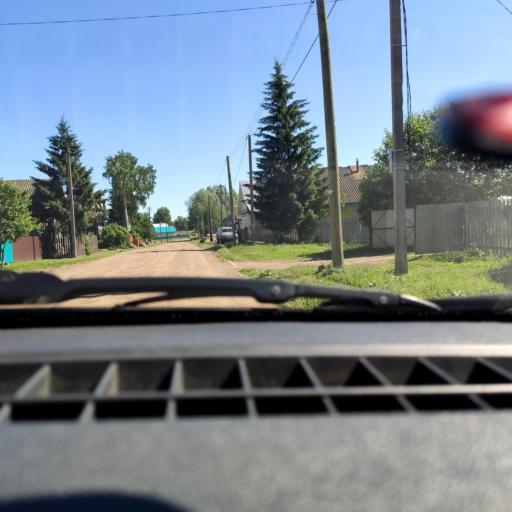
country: RU
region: Bashkortostan
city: Iglino
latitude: 54.8985
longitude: 56.4922
